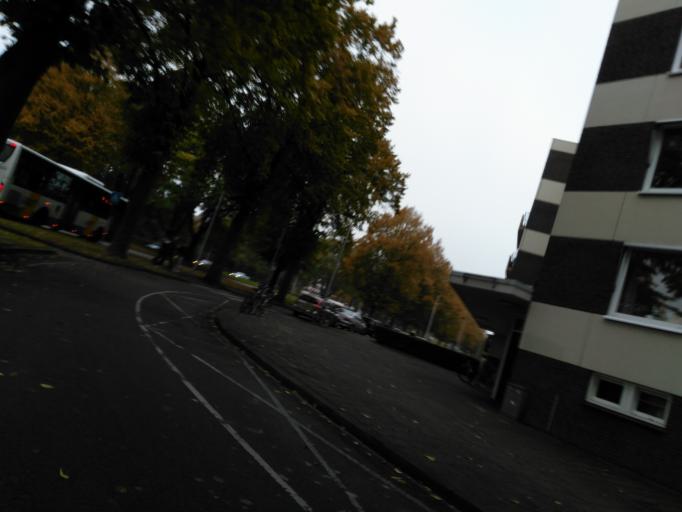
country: NL
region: Limburg
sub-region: Gemeente Maastricht
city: Maastricht
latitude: 50.8491
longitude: 5.6725
